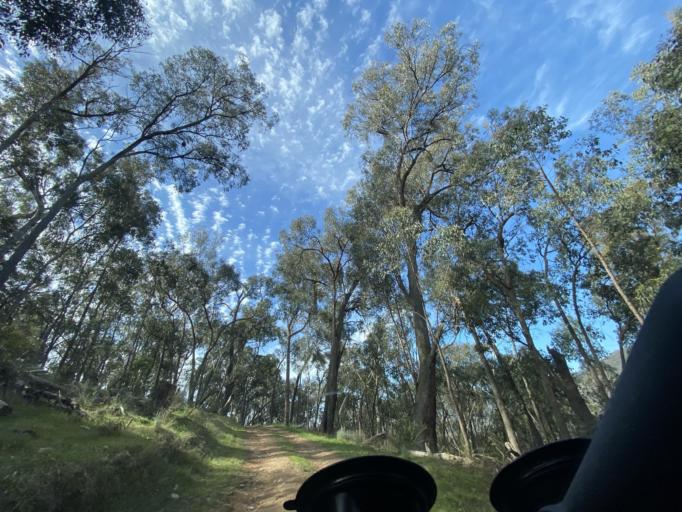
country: AU
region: Victoria
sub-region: Mansfield
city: Mansfield
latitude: -36.8071
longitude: 146.1193
